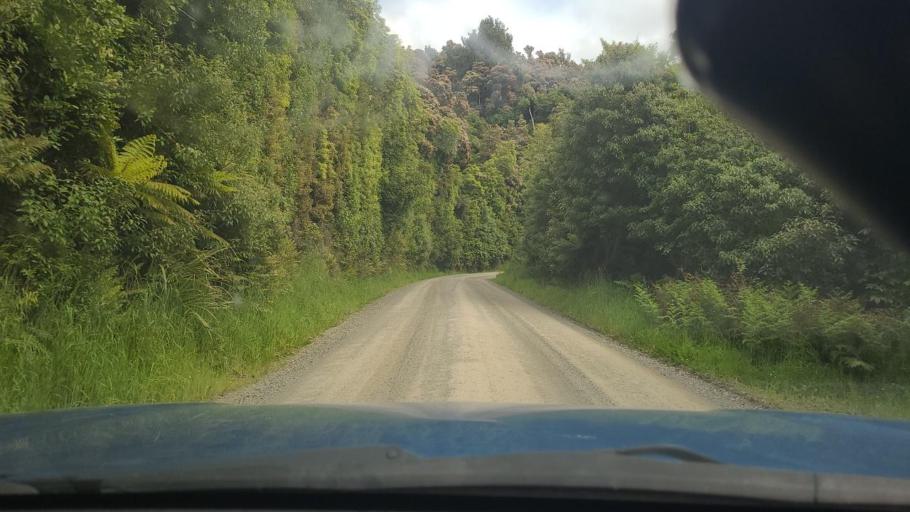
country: NZ
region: Otago
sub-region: Clutha District
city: Papatowai
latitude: -46.4902
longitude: 169.1541
